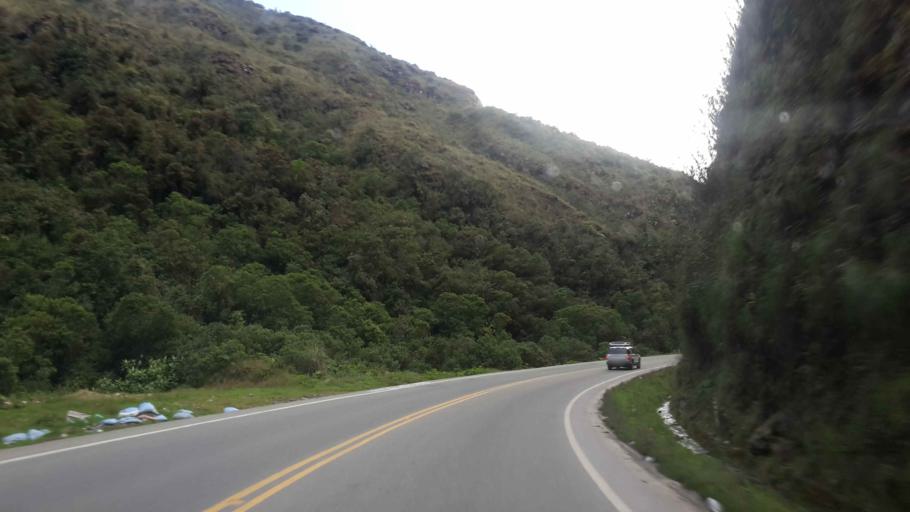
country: BO
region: Cochabamba
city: Colomi
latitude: -17.2111
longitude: -65.8885
